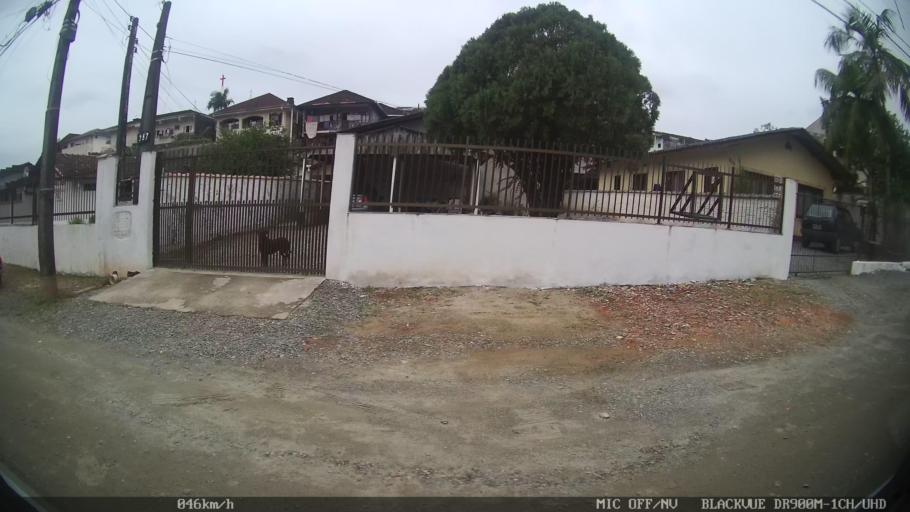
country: BR
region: Santa Catarina
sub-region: Joinville
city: Joinville
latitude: -26.2676
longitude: -48.8871
